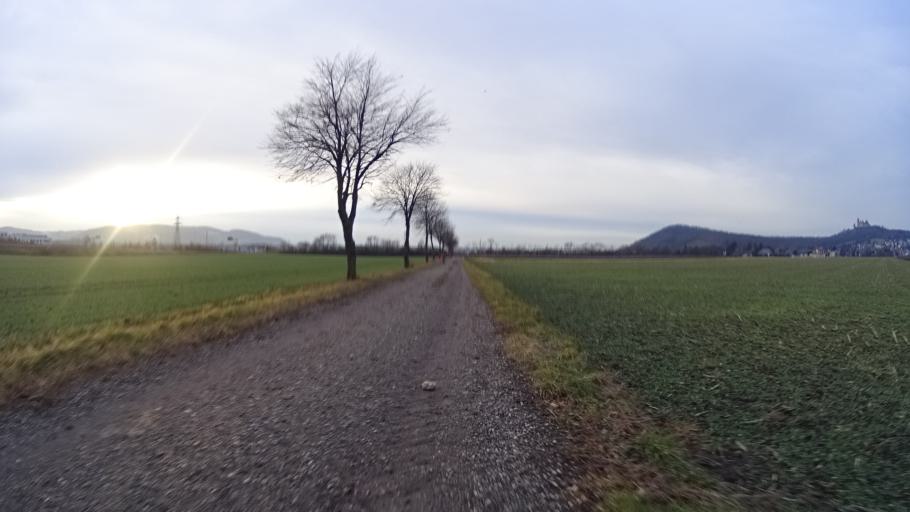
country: AT
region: Lower Austria
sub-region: Politischer Bezirk Korneuburg
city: Leobendorf
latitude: 48.3655
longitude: 16.3202
